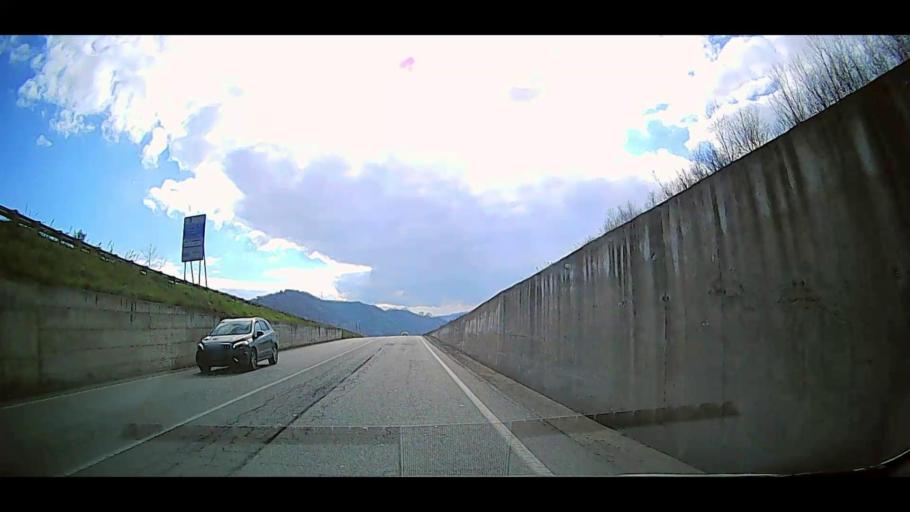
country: IT
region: Calabria
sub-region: Provincia di Cosenza
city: Cosenza
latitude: 39.3094
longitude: 16.2624
